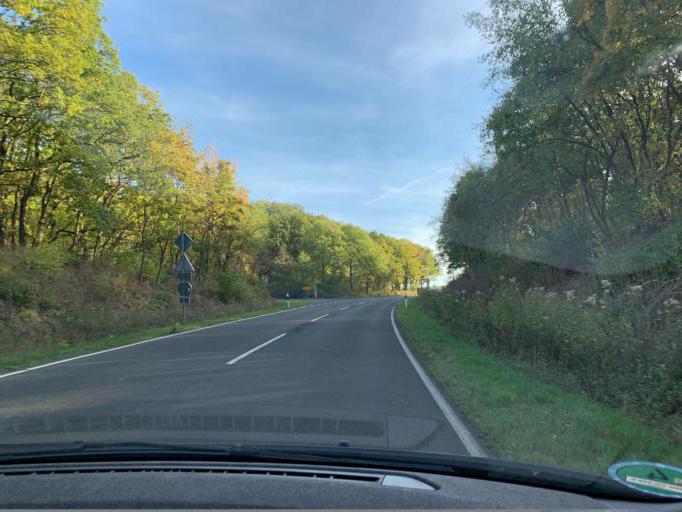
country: DE
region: North Rhine-Westphalia
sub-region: Regierungsbezirk Koln
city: Kreuzau
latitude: 50.7200
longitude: 6.5173
